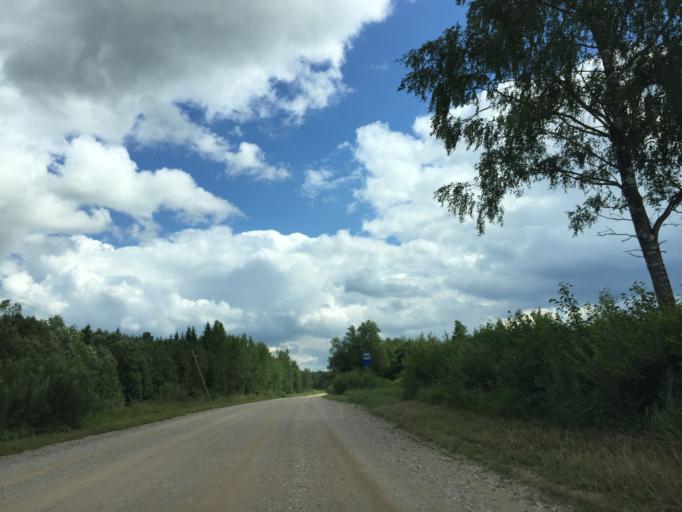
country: LV
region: Malpils
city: Malpils
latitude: 56.8765
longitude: 24.9996
